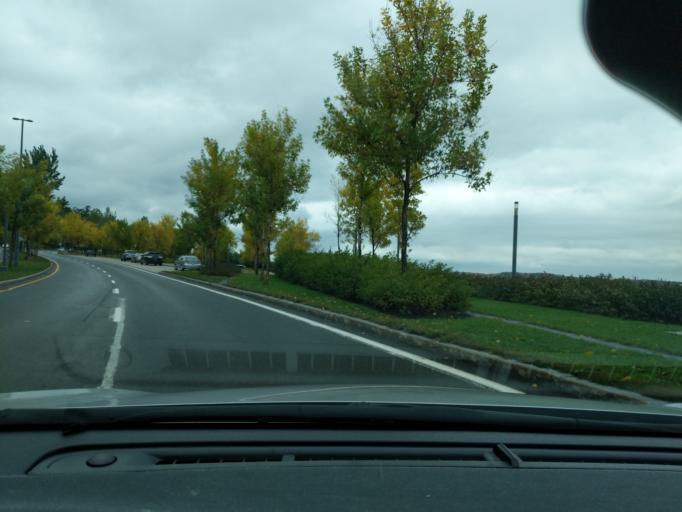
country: CA
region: Quebec
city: Quebec
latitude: 46.7558
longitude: -71.2723
